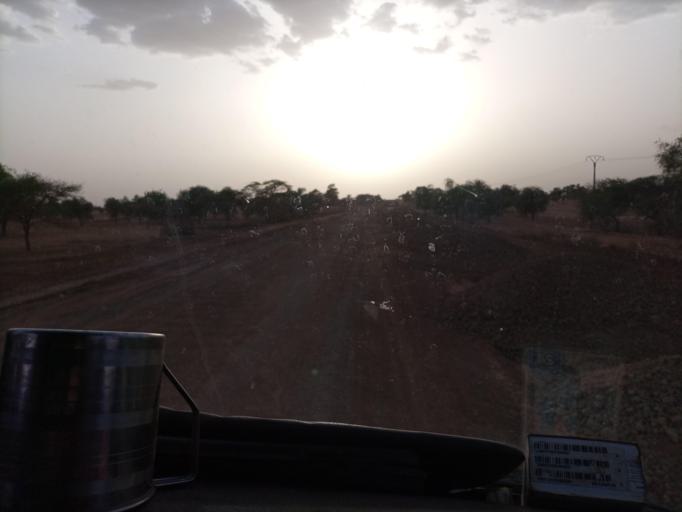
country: SN
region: Louga
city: Dara
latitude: 15.3840
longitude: -15.6209
